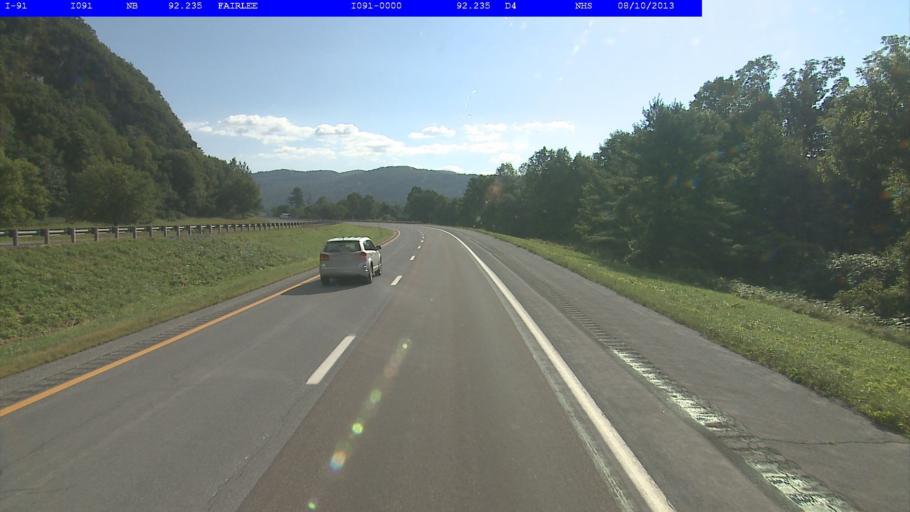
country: US
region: New Hampshire
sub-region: Grafton County
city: Orford
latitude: 43.9098
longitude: -72.1399
